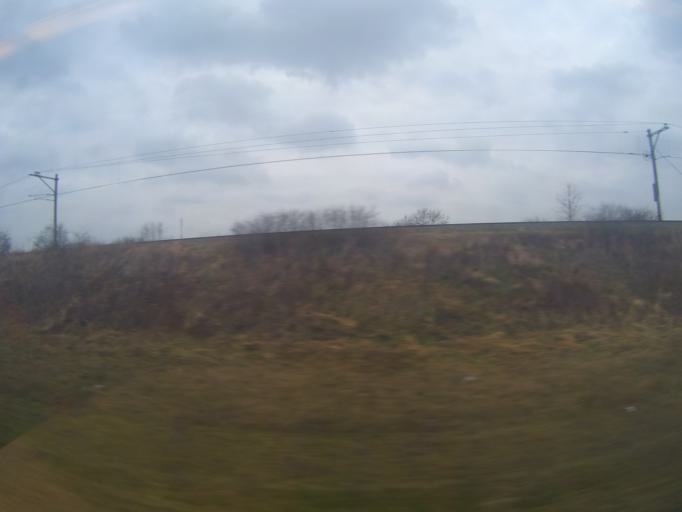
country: NL
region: Utrecht
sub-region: Gemeente De Bilt
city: De Bilt
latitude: 52.1166
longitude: 5.1542
